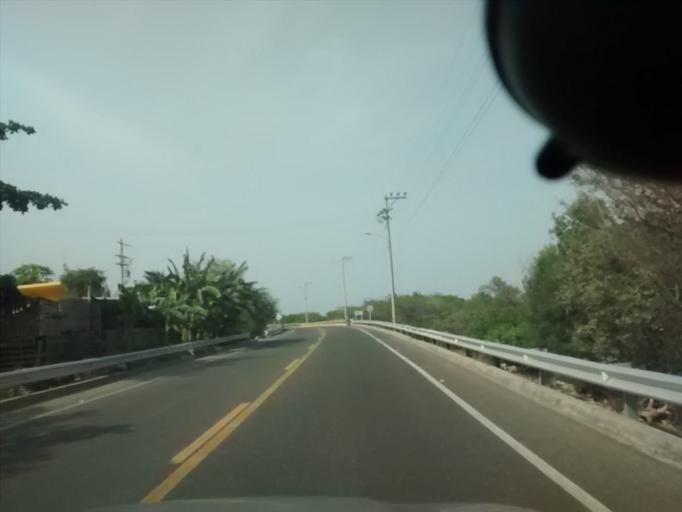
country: CO
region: Bolivar
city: Cartagena
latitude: 10.4779
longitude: -75.4904
